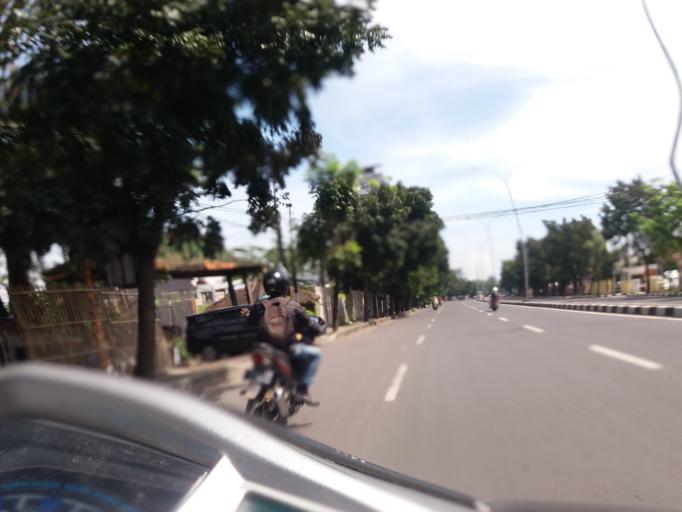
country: ID
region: West Java
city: Bandung
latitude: -6.9487
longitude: 107.6315
